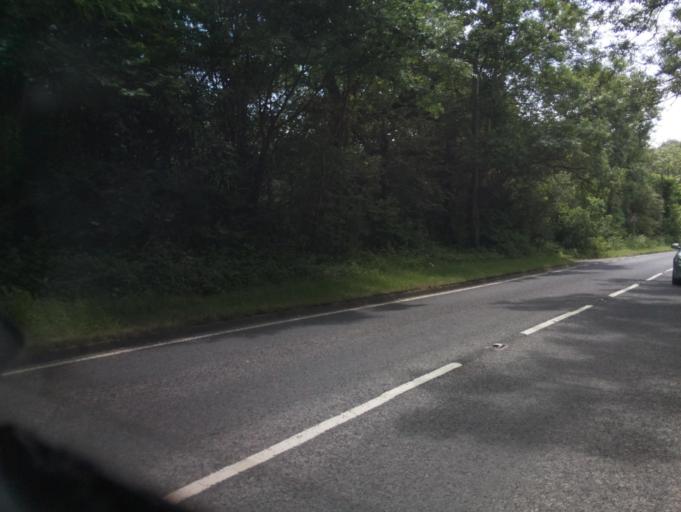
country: GB
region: Wales
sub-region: Bridgend county borough
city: Merthyr Mawr
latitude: 51.4800
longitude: -3.5853
